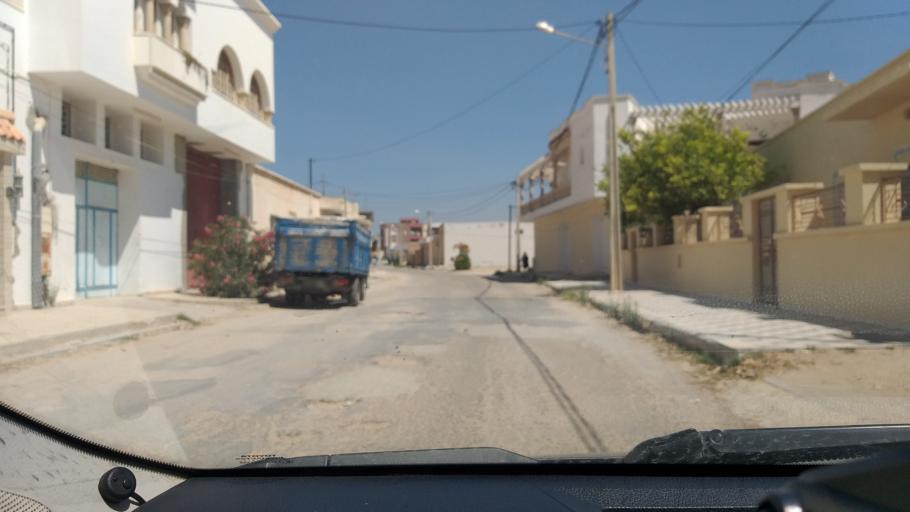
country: TN
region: Al Mahdiyah
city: El Jem
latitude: 35.2932
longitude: 10.7122
